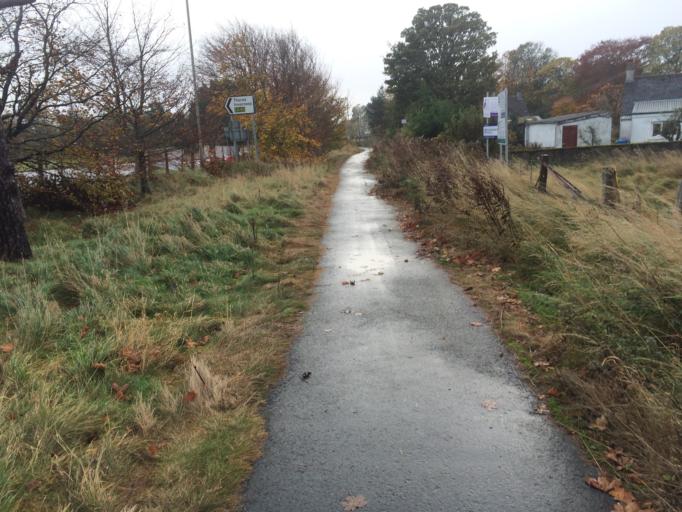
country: GB
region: Scotland
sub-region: Highland
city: Alness
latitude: 57.6917
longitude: -4.2430
